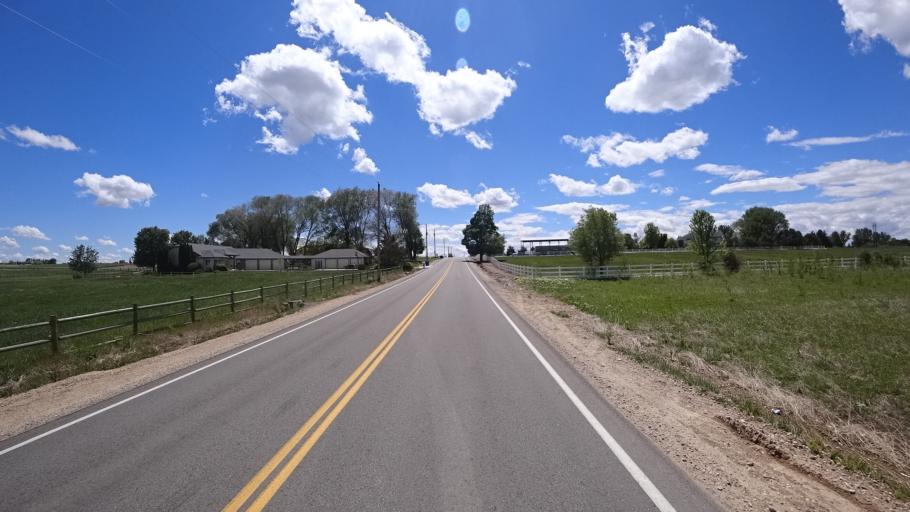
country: US
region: Idaho
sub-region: Ada County
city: Meridian
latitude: 43.5736
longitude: -116.4537
